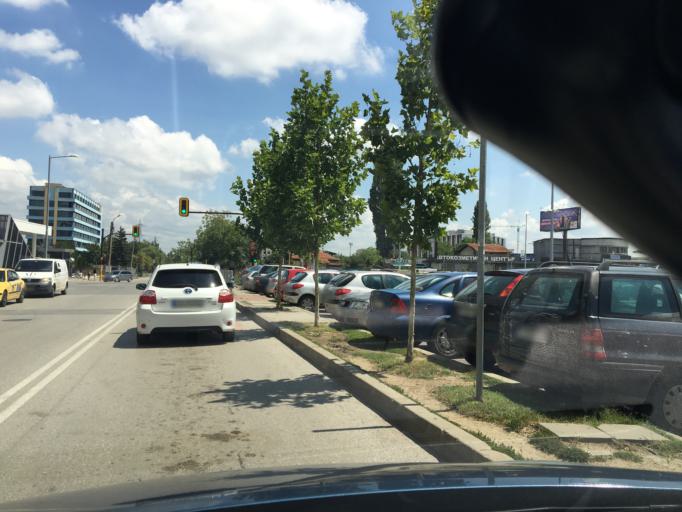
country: BG
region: Sofia-Capital
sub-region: Stolichna Obshtina
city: Sofia
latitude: 42.6569
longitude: 23.3151
